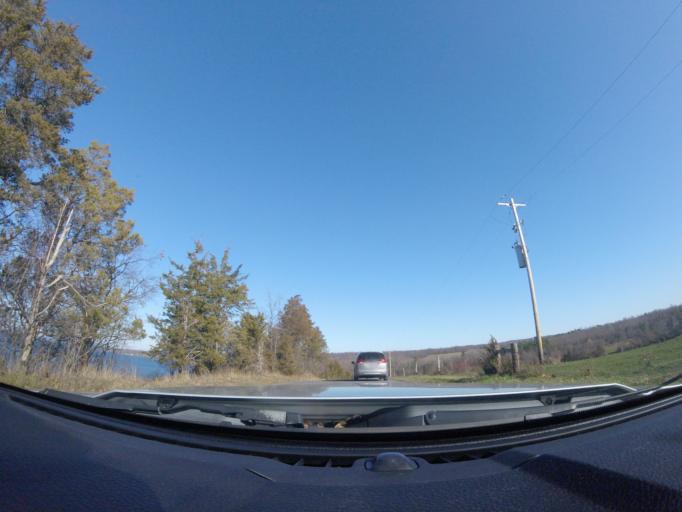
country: US
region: New York
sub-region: Cayuga County
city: Union Springs
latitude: 42.7337
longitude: -76.7064
